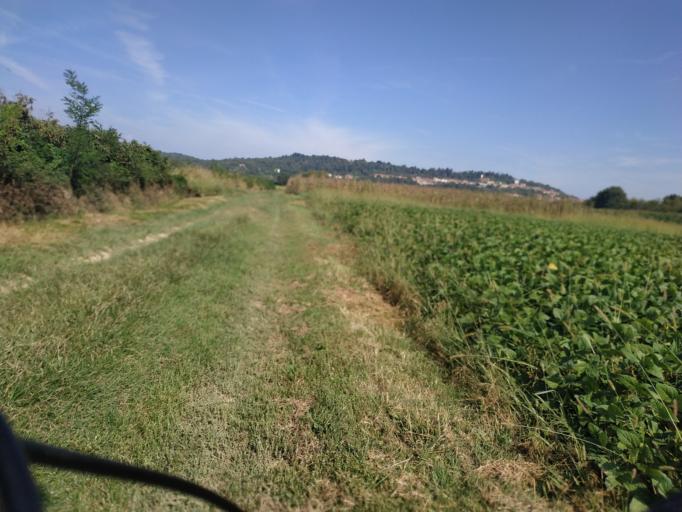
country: IT
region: Piedmont
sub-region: Provincia di Torino
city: Orio Canavese
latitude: 45.3180
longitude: 7.8503
